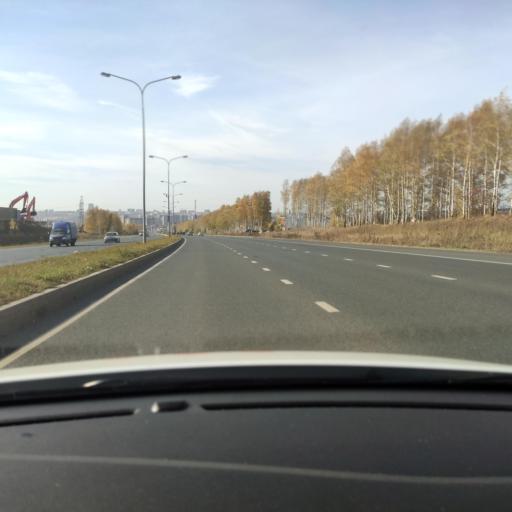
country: RU
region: Tatarstan
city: Vysokaya Gora
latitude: 55.8017
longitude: 49.2890
